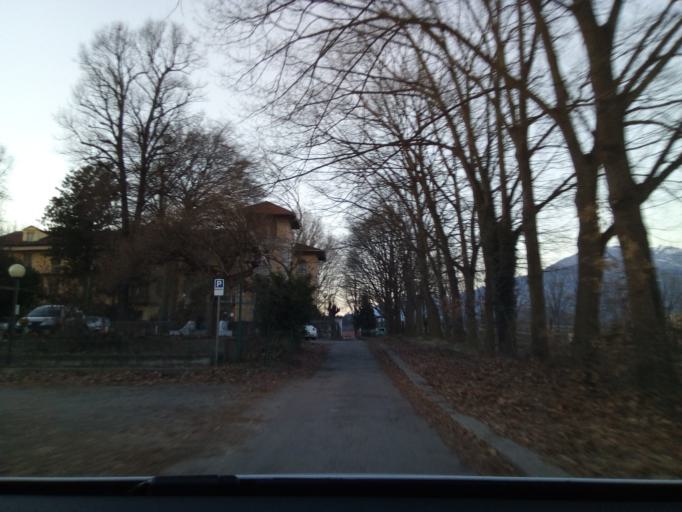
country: IT
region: Piedmont
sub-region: Provincia di Torino
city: Cascinette d'Ivrea
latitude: 45.4720
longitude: 7.8997
